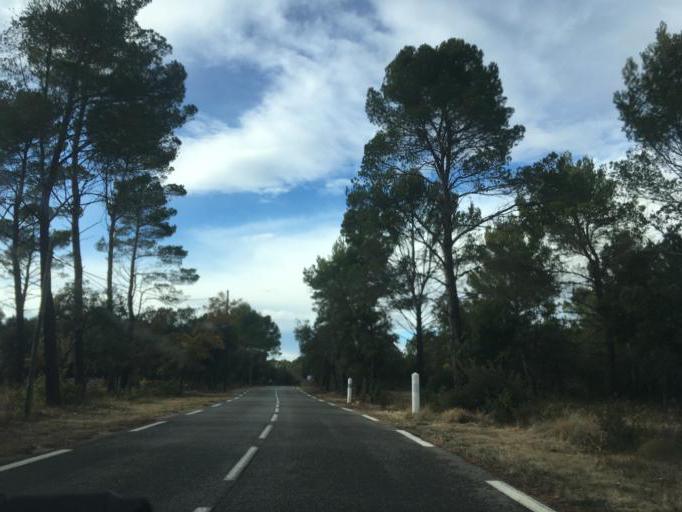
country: FR
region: Provence-Alpes-Cote d'Azur
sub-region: Departement du Var
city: Aups
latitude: 43.6121
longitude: 6.2303
